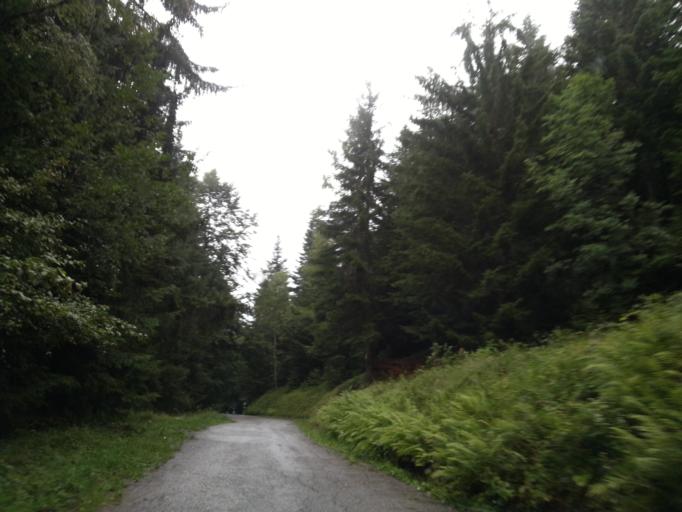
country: FR
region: Rhone-Alpes
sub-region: Departement de la Savoie
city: Marthod
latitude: 45.6995
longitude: 6.4495
